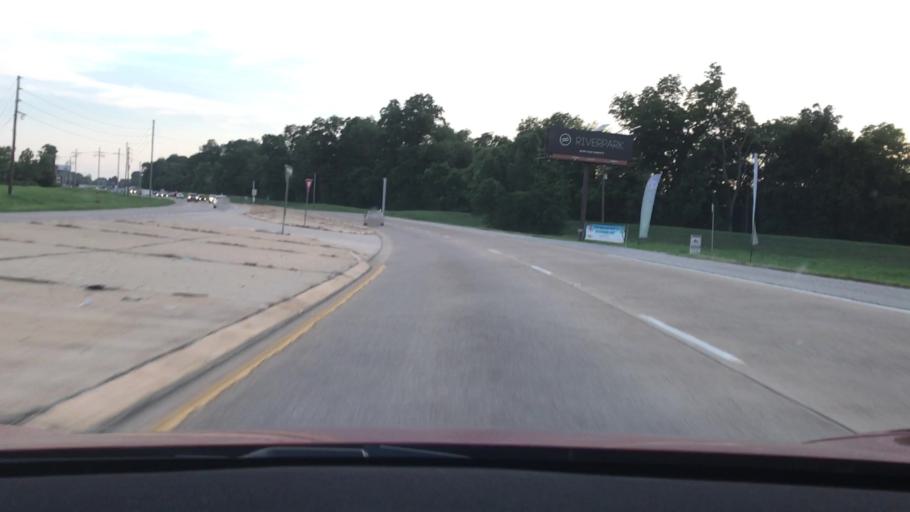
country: US
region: Louisiana
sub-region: Bossier Parish
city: Bossier City
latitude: 32.4580
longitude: -93.6890
